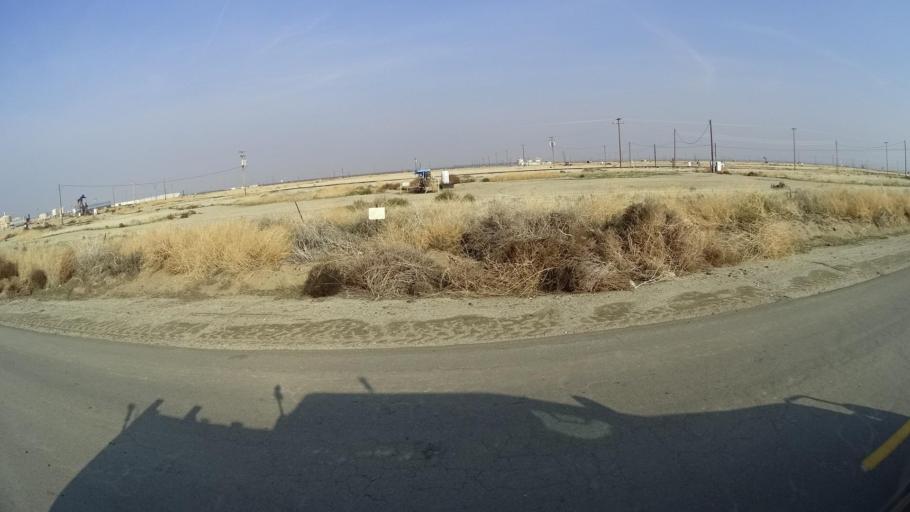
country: US
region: California
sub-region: Kern County
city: Lebec
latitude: 34.9844
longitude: -118.9270
